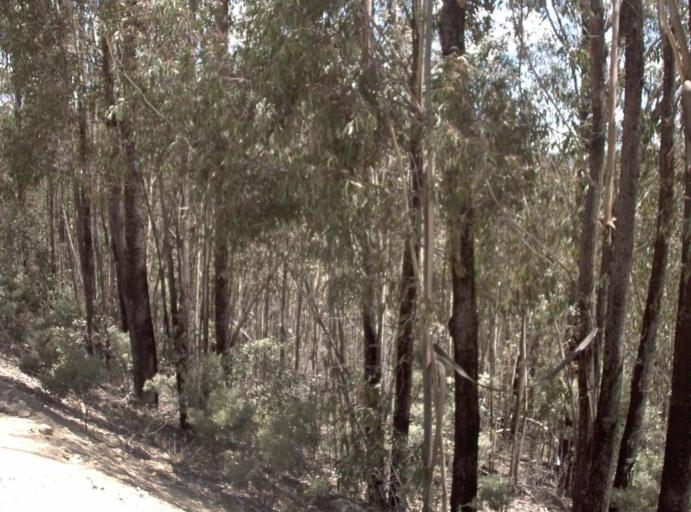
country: AU
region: New South Wales
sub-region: Snowy River
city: Jindabyne
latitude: -37.0785
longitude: 148.3287
